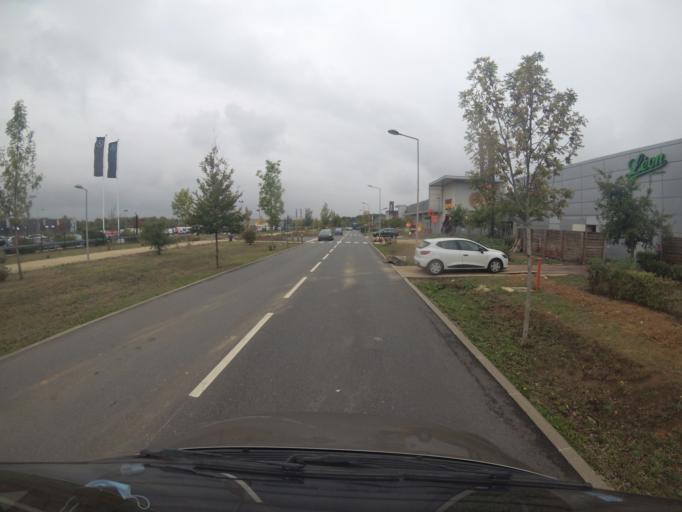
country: FR
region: Ile-de-France
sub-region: Departement de Seine-et-Marne
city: Chanteloup-en-Brie
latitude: 48.8538
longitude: 2.7580
